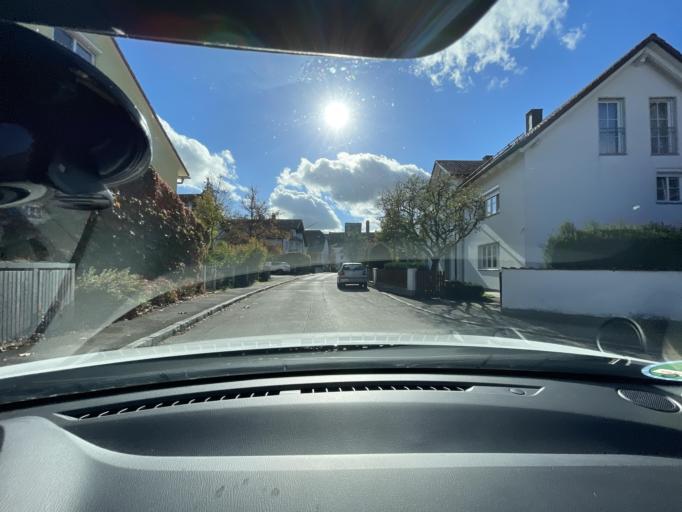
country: DE
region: Bavaria
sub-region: Upper Bavaria
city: Maisach
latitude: 48.2183
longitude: 11.2634
